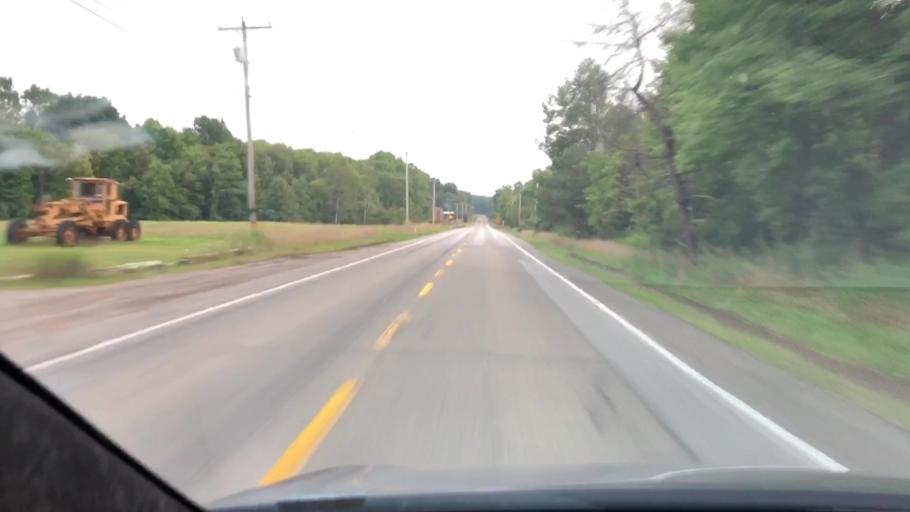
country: US
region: Pennsylvania
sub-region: Butler County
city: Slippery Rock
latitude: 41.0387
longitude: -80.0067
